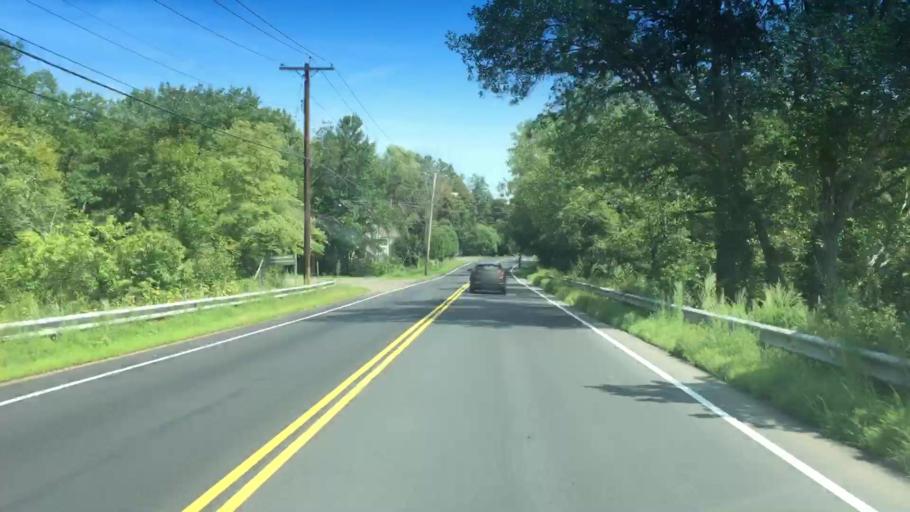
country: US
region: Massachusetts
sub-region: Norfolk County
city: Medfield
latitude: 42.1804
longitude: -71.3231
